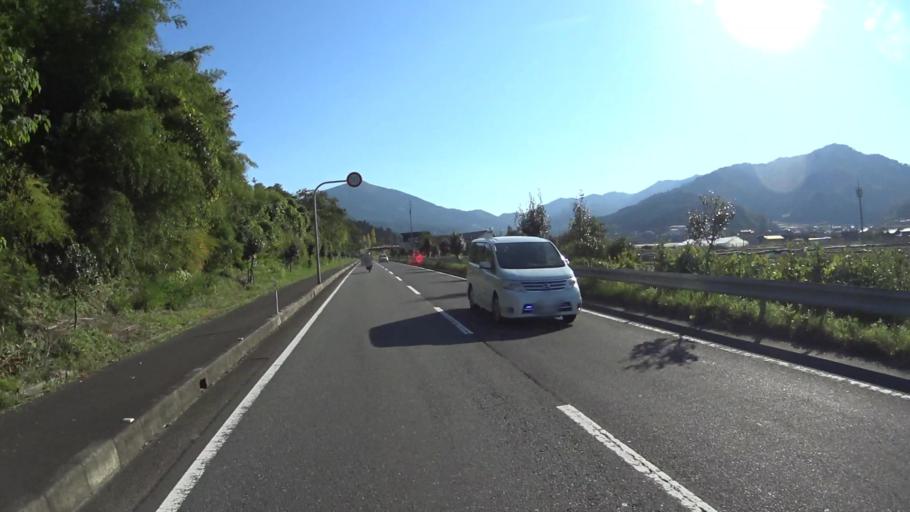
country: JP
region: Kyoto
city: Miyazu
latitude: 35.4847
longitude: 135.0940
